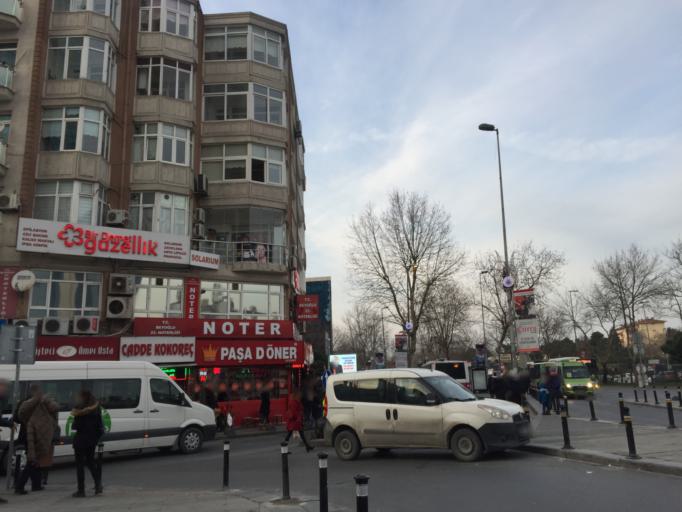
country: TR
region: Istanbul
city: Sisli
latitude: 41.0868
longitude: 29.0066
